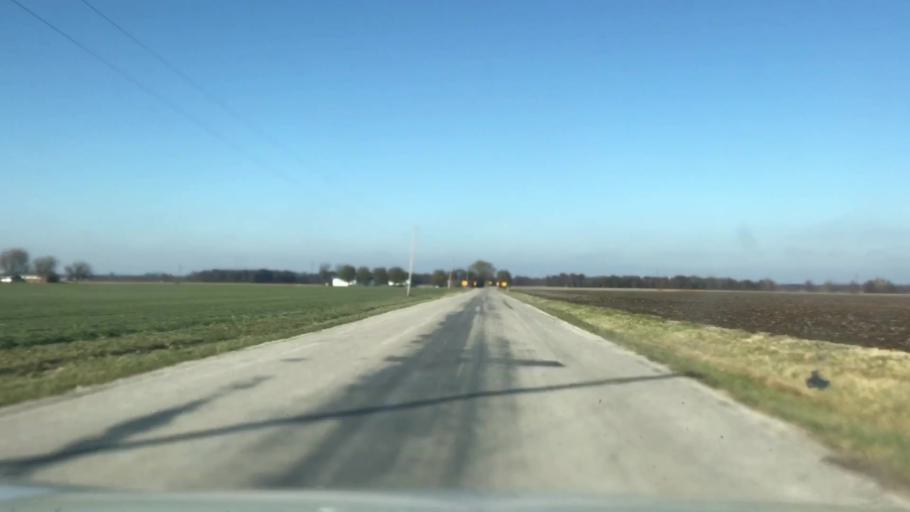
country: US
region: Illinois
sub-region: Washington County
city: Okawville
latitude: 38.4382
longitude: -89.4779
